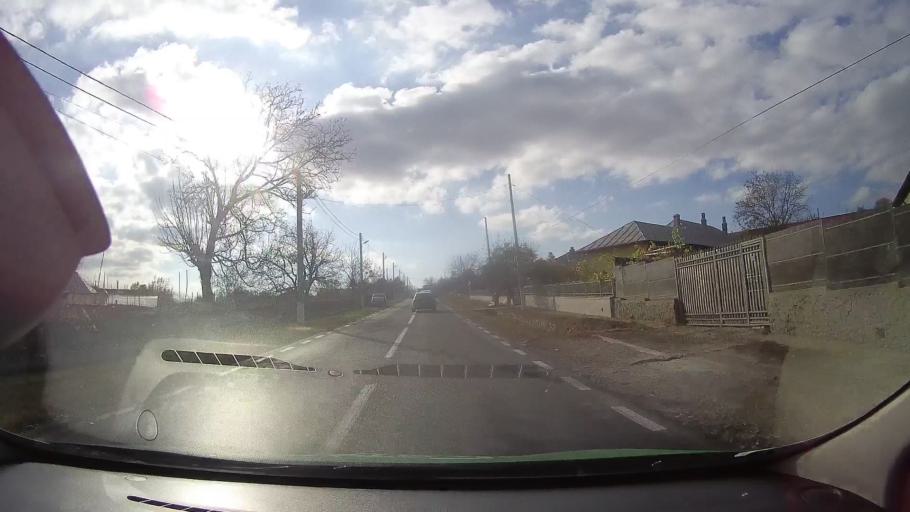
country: RO
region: Tulcea
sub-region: Comuna Topolog
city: Topolog
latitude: 44.8732
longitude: 28.3718
